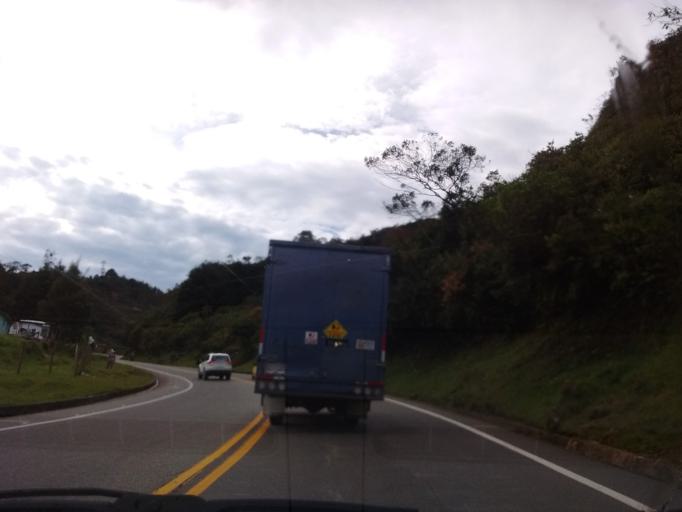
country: CO
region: Antioquia
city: Santuario
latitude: 6.1015
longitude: -75.2274
